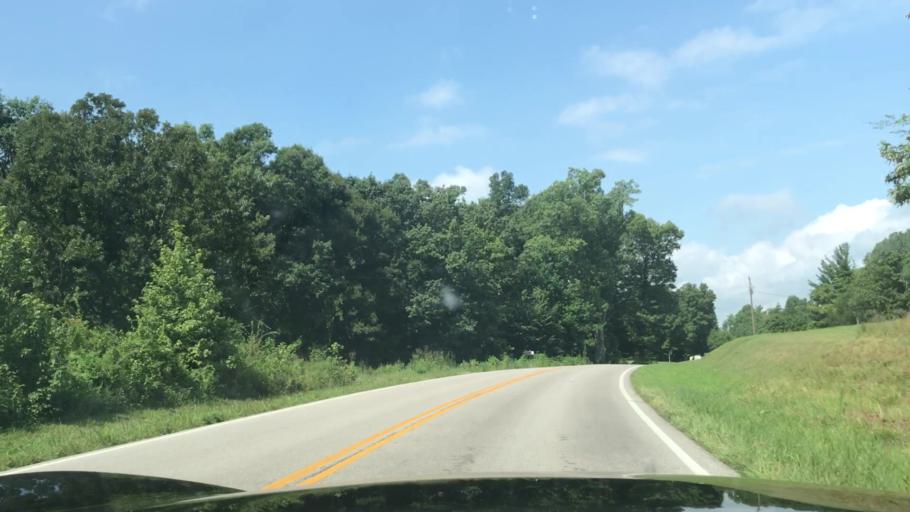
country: US
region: Kentucky
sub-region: Butler County
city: Morgantown
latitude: 37.1804
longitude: -86.8586
